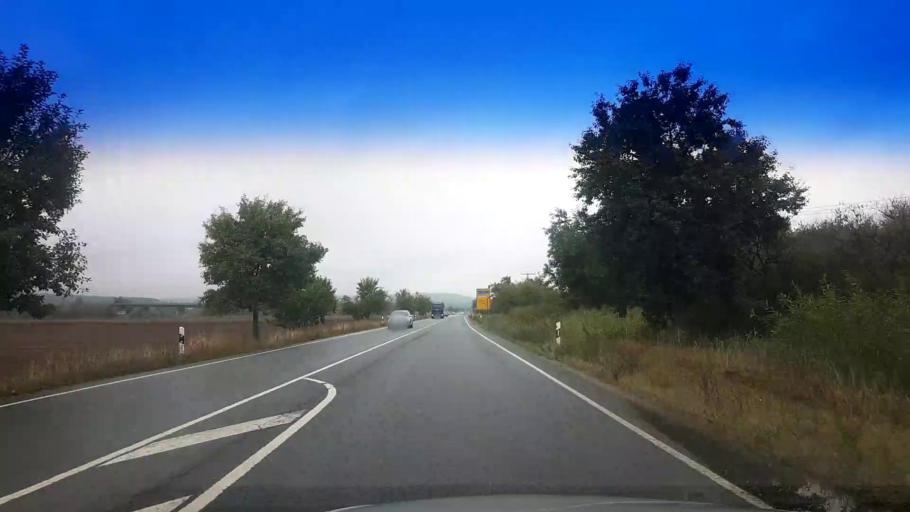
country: DE
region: Bavaria
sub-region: Upper Franconia
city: Eggolsheim
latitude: 49.7657
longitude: 11.0411
